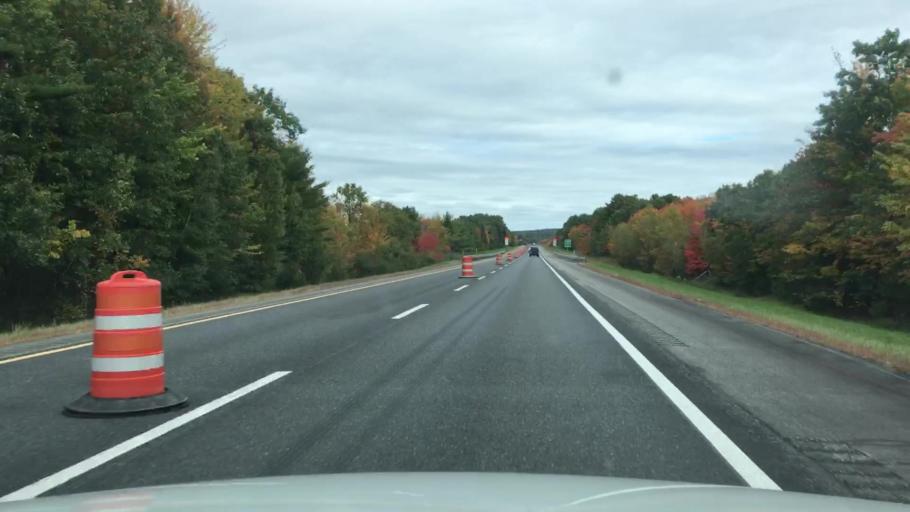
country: US
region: Maine
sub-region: Sagadahoc County
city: Richmond
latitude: 44.1359
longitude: -69.8442
